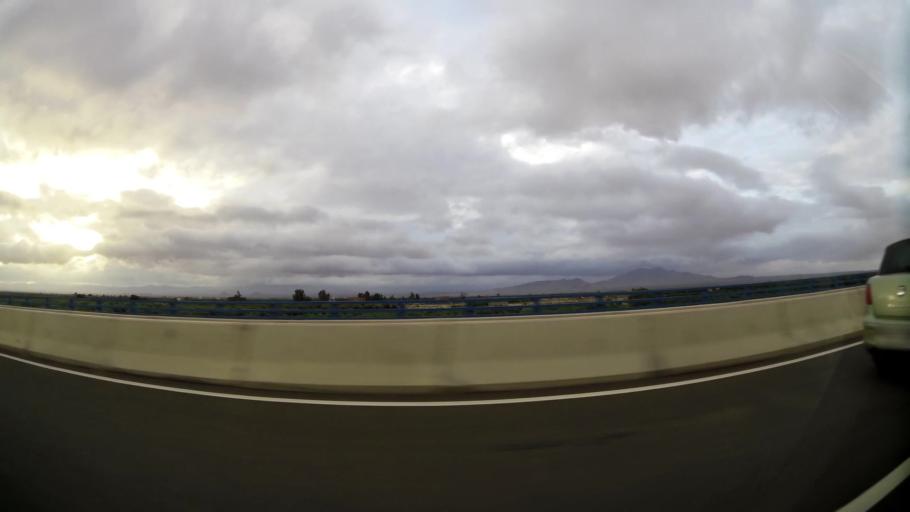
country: MA
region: Taza-Al Hoceima-Taounate
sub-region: Taza
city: Guercif
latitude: 34.3624
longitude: -3.2918
